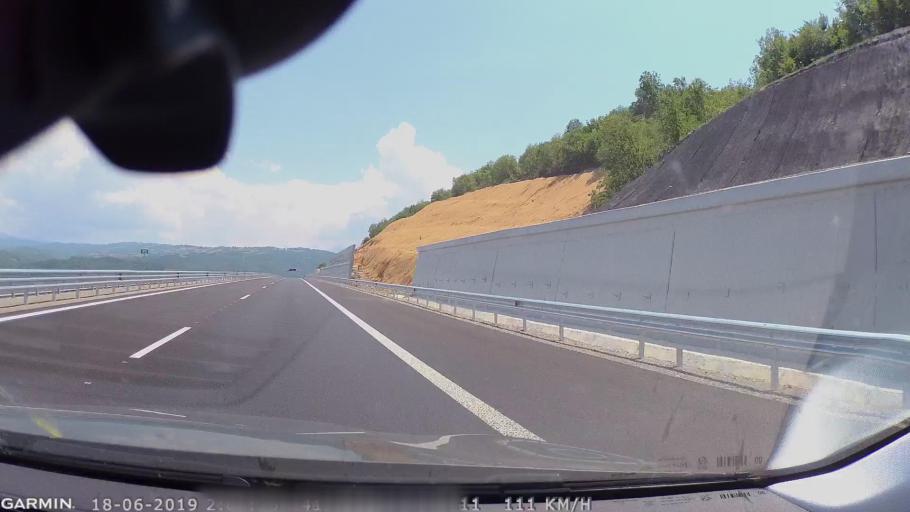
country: BG
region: Blagoevgrad
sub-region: Obshtina Blagoevgrad
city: Blagoevgrad
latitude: 41.9756
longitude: 23.0730
